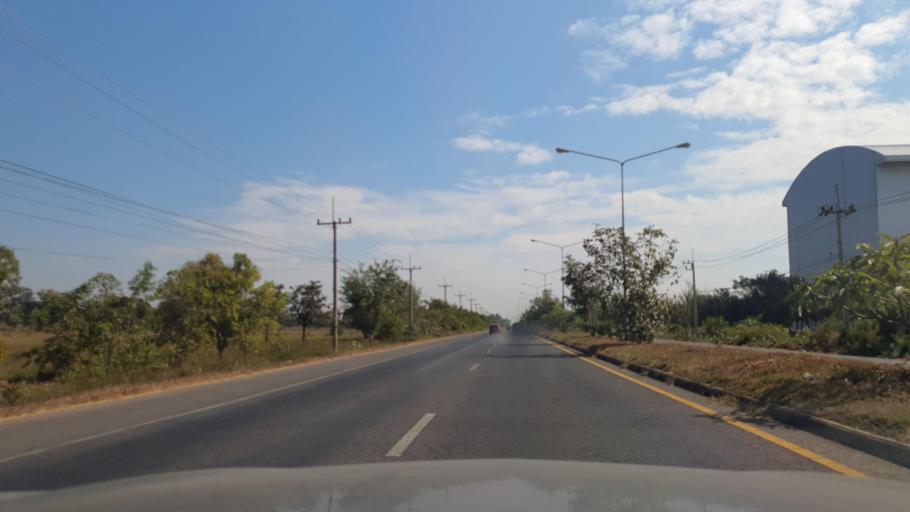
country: TH
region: Maha Sarakham
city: Kantharawichai
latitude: 16.3836
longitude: 103.2233
